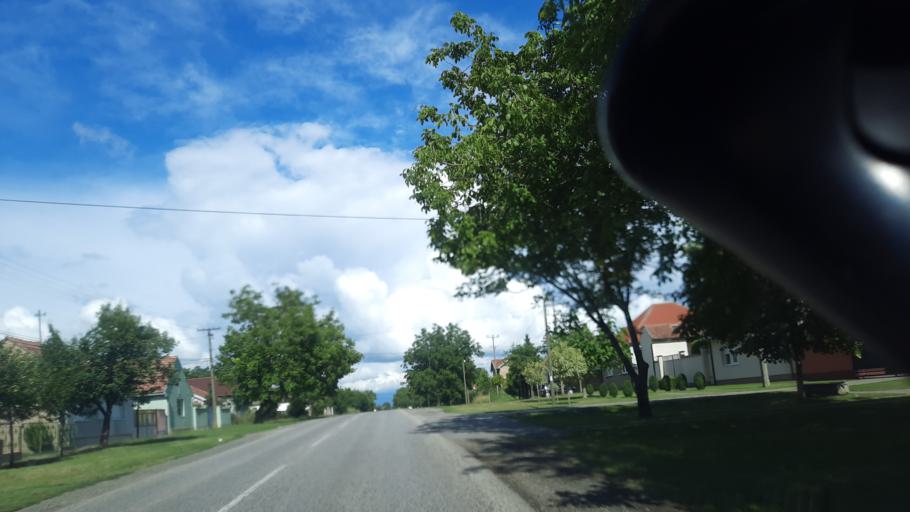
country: RS
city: Sasinci
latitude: 45.0054
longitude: 19.7672
